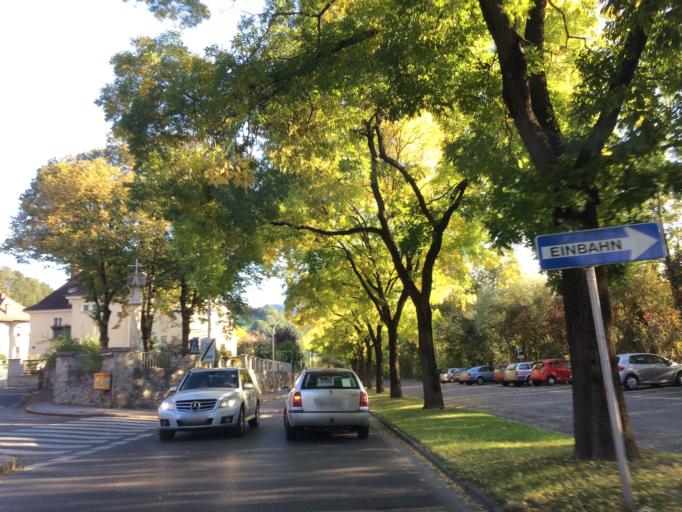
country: AT
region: Styria
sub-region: Politischer Bezirk Leoben
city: Leoben
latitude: 47.3753
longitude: 15.0953
